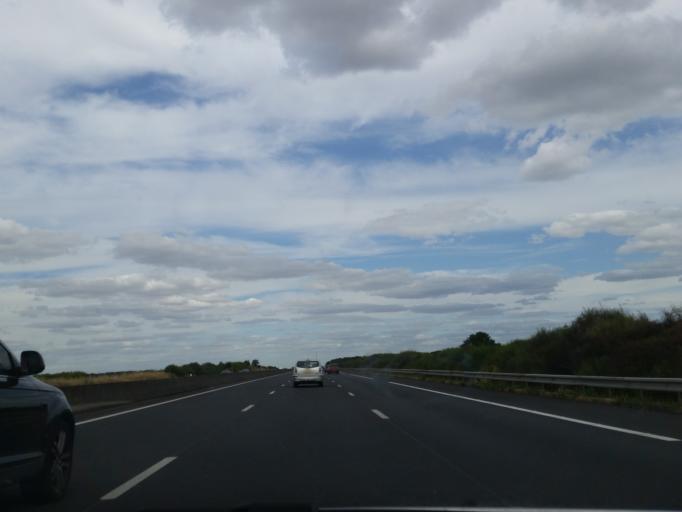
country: FR
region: Centre
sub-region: Departement d'Indre-et-Loire
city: Auzouer-en-Touraine
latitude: 47.5525
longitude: 1.0055
